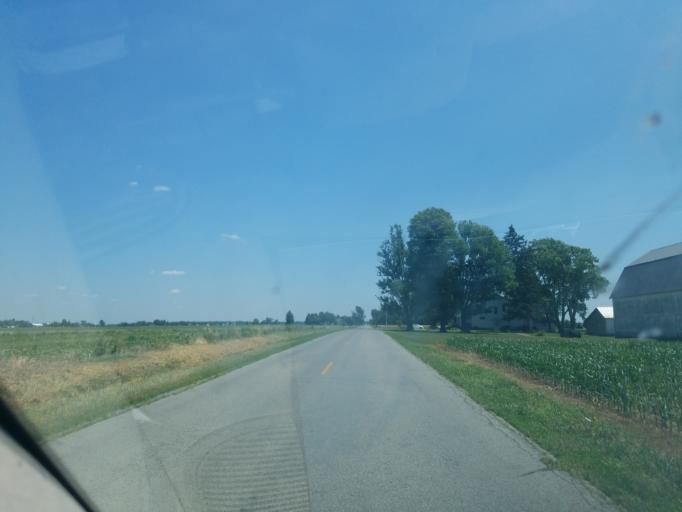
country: US
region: Ohio
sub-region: Allen County
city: Elida
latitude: 40.7871
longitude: -84.2749
